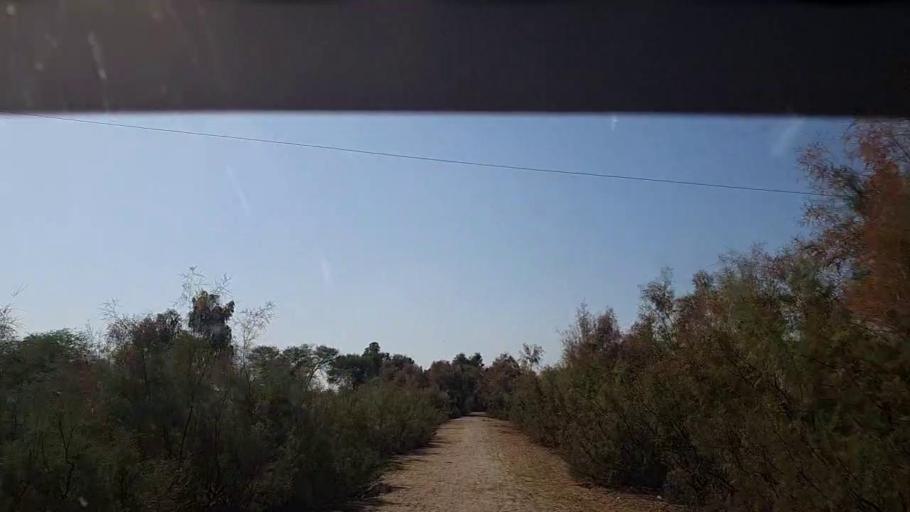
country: PK
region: Sindh
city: Ghauspur
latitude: 28.1798
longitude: 69.0283
